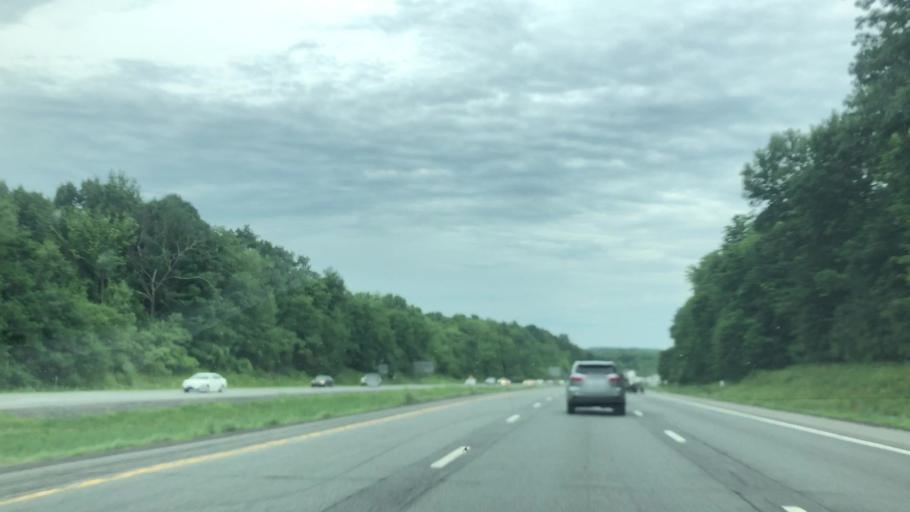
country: US
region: New York
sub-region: Saratoga County
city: Country Knolls
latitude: 42.9605
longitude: -73.8016
